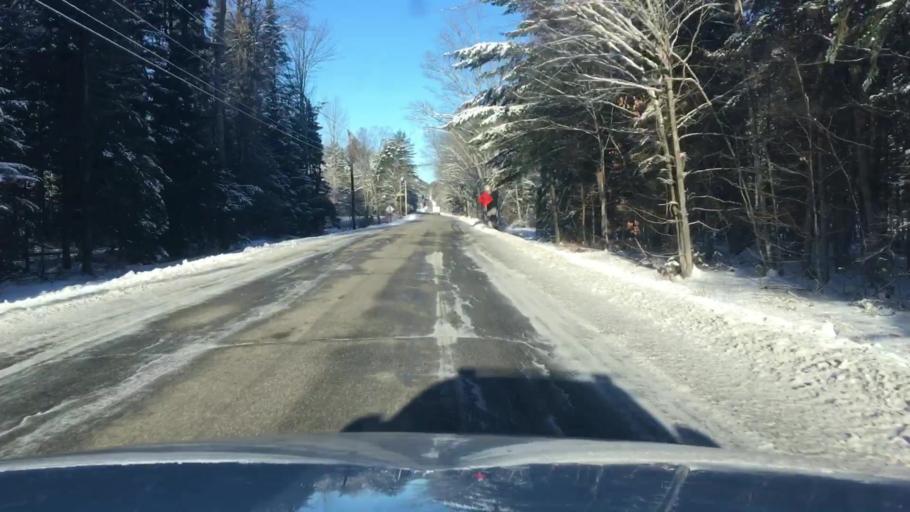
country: US
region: Maine
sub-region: Kennebec County
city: Belgrade
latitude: 44.4100
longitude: -69.8659
